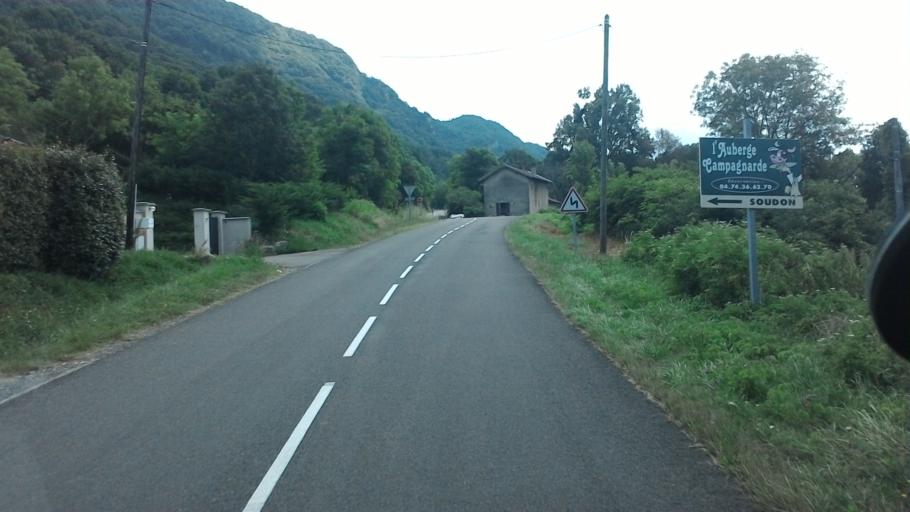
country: FR
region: Rhone-Alpes
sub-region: Departement de l'Ain
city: Lagnieu
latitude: 45.8937
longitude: 5.3587
